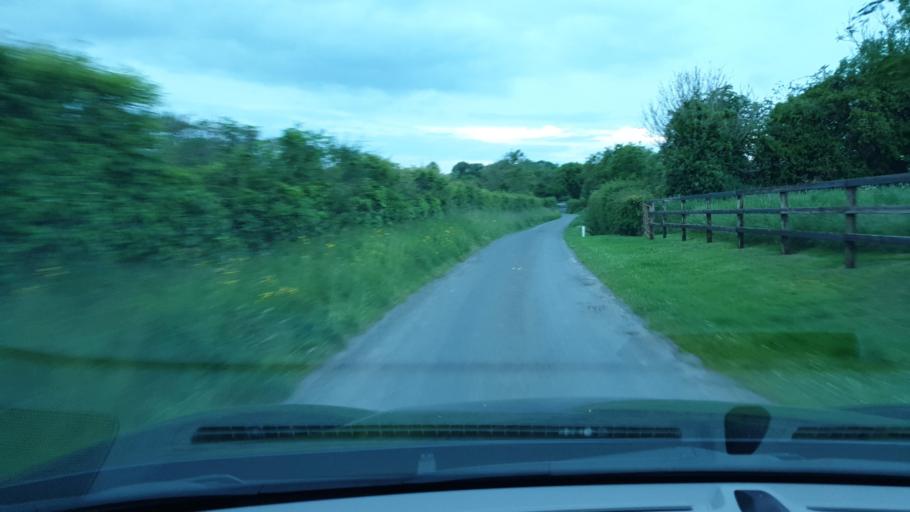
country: IE
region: Leinster
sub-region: An Mhi
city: Ashbourne
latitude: 53.5867
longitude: -6.3661
